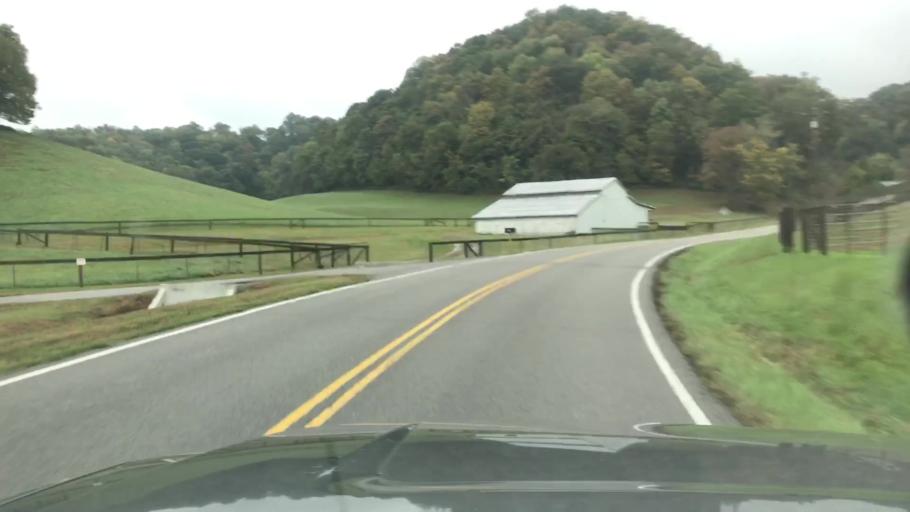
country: US
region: Tennessee
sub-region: Williamson County
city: Brentwood Estates
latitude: 35.9973
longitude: -86.8285
